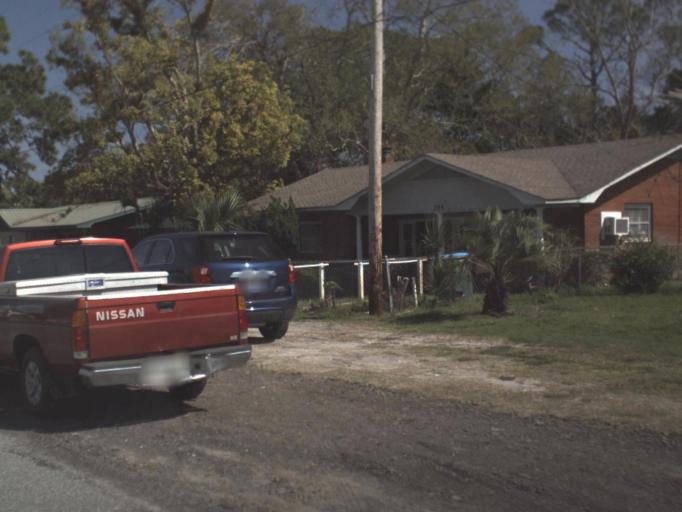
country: US
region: Florida
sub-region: Franklin County
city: Eastpoint
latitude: 29.7364
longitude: -84.8844
